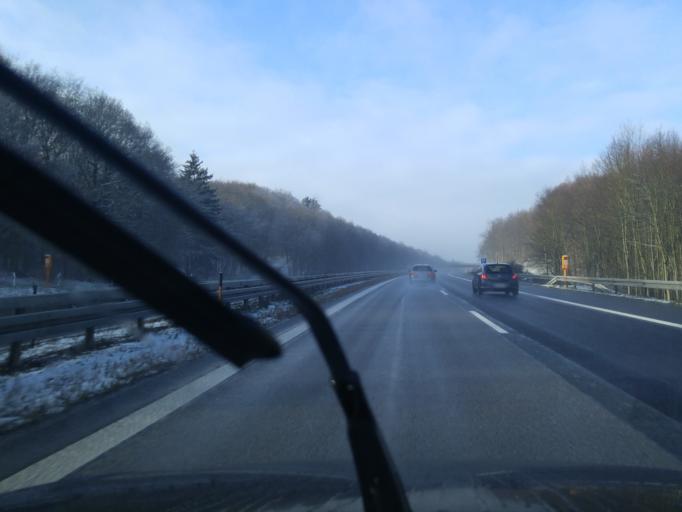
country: DE
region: Bavaria
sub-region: Regierungsbezirk Unterfranken
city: Wasserlosen
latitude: 50.0740
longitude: 10.0212
